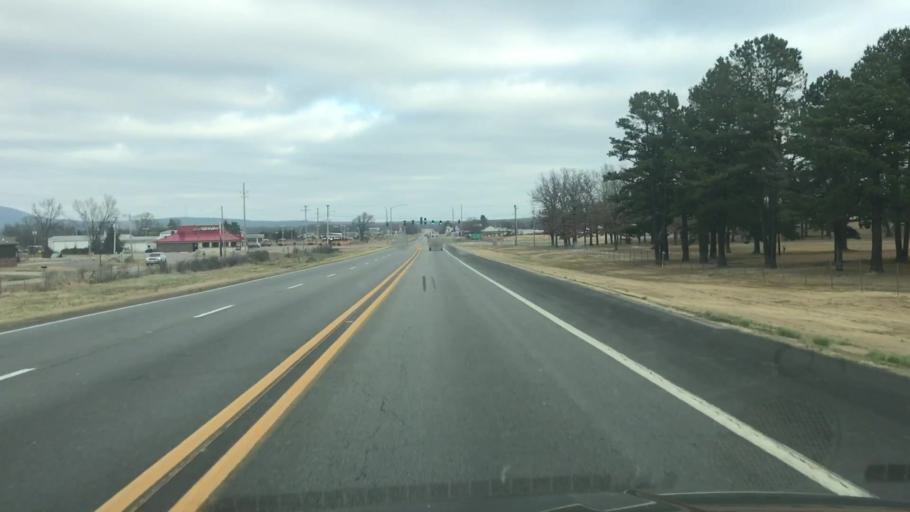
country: US
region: Arkansas
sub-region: Scott County
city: Waldron
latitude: 34.8945
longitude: -94.1076
